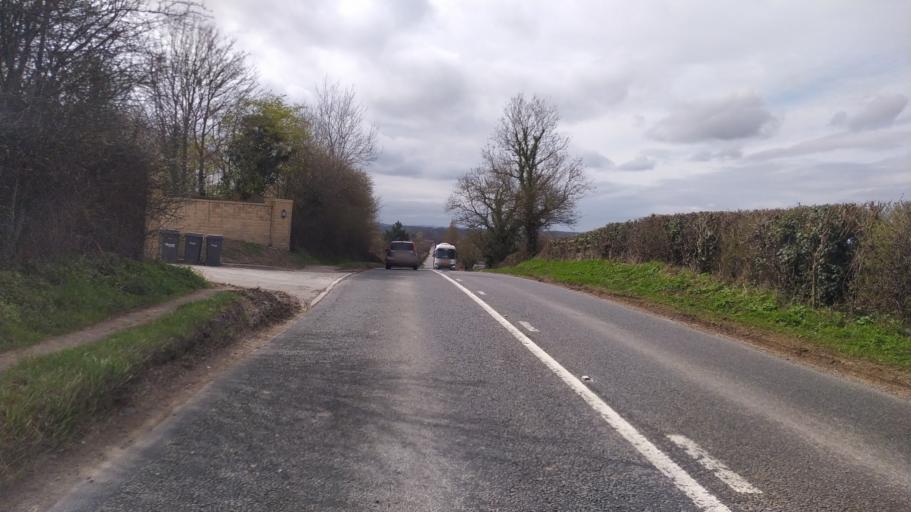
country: GB
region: England
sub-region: Wiltshire
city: North Bradley
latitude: 51.2991
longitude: -2.1806
